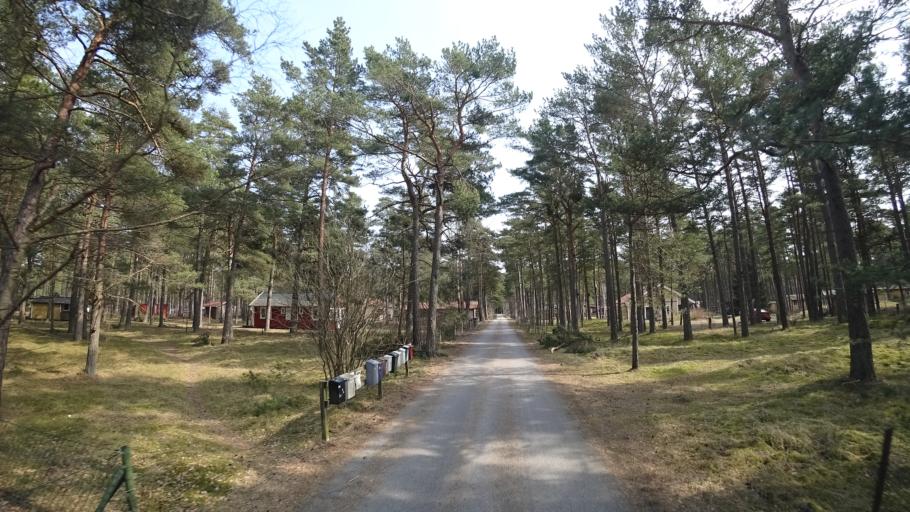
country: SE
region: Skane
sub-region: Kristianstads Kommun
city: Ahus
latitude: 55.9455
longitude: 14.3170
